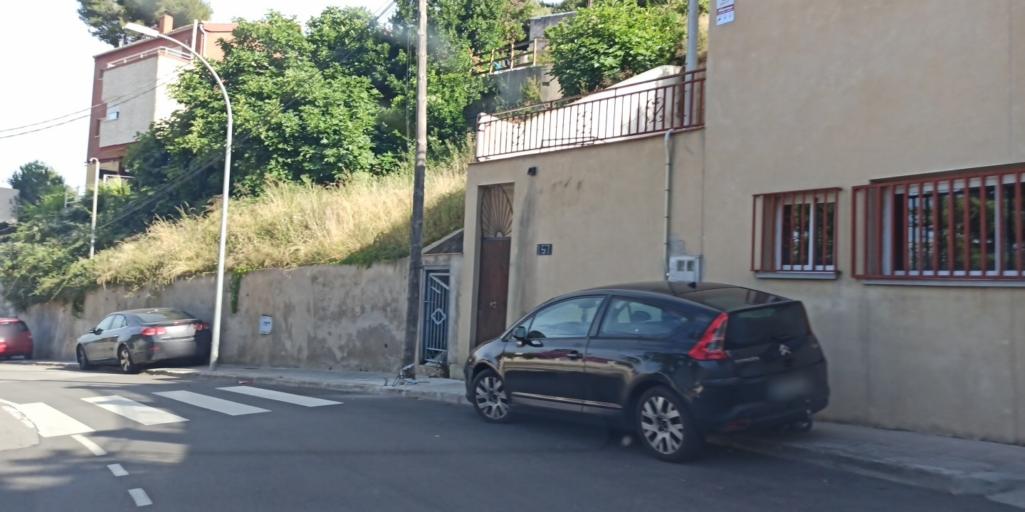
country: ES
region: Catalonia
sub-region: Provincia de Barcelona
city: Santa Coloma de Cervello
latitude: 41.3618
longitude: 1.9995
